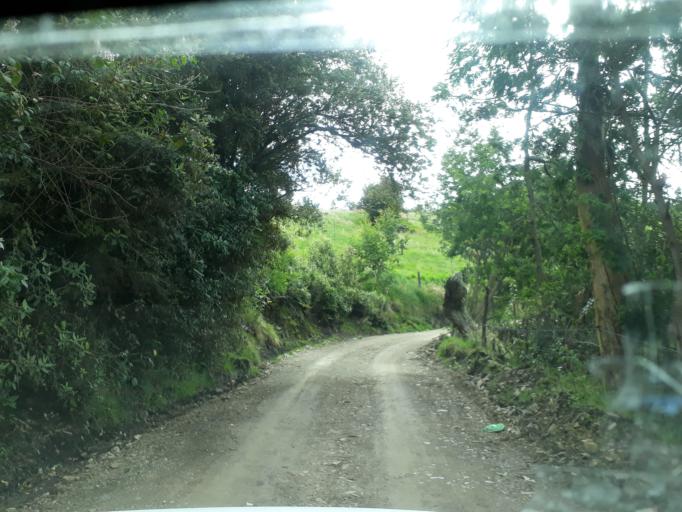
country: CO
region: Cundinamarca
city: La Mesa
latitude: 5.2478
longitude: -73.8934
